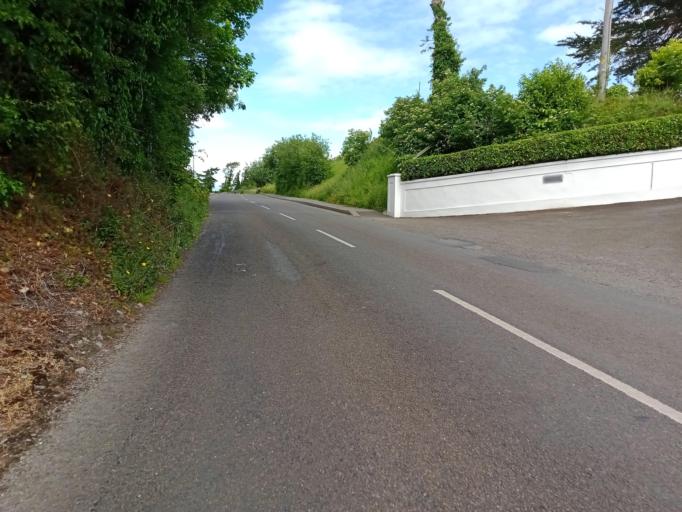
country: IE
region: Leinster
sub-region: Kilkenny
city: Kilkenny
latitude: 52.6753
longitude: -7.2490
